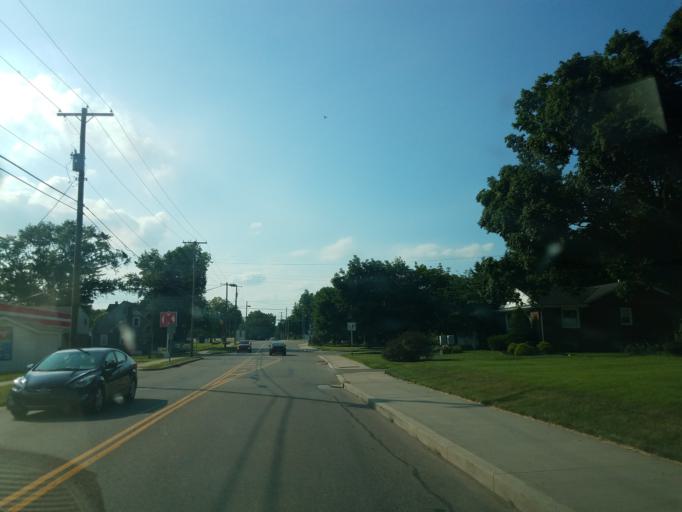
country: US
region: Ohio
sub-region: Stark County
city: Canal Fulton
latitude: 40.8902
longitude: -81.5950
